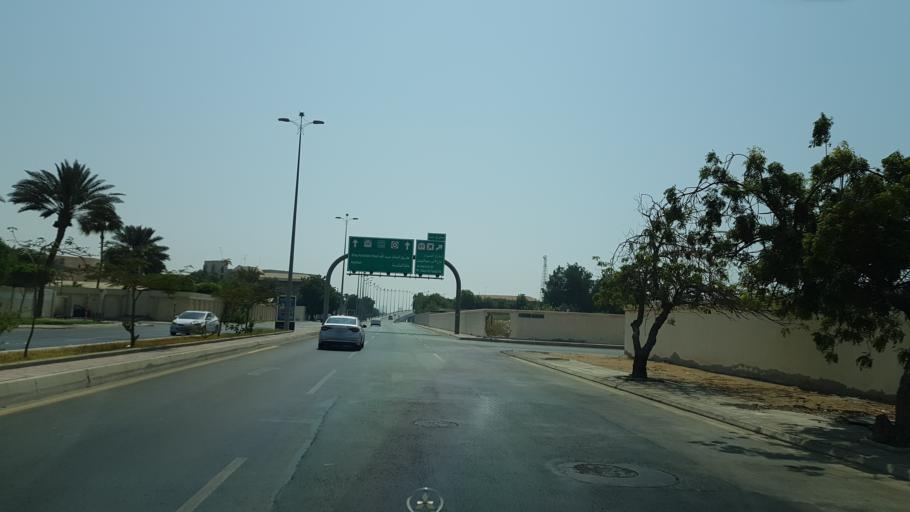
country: SA
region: Makkah
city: Jeddah
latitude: 21.5462
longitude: 39.1534
